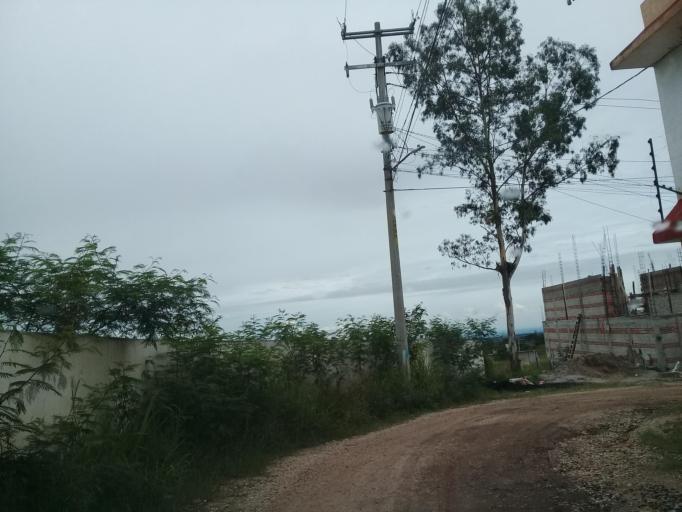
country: MX
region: Veracruz
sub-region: Emiliano Zapata
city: Jacarandas
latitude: 19.4966
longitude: -96.8428
